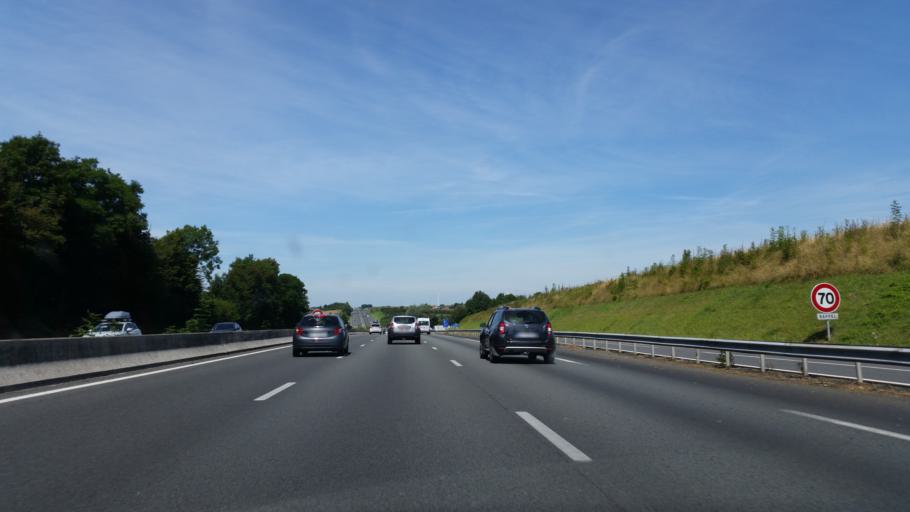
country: FR
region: Nord-Pas-de-Calais
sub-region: Departement du Pas-de-Calais
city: Croisilles
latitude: 50.1870
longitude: 2.8734
